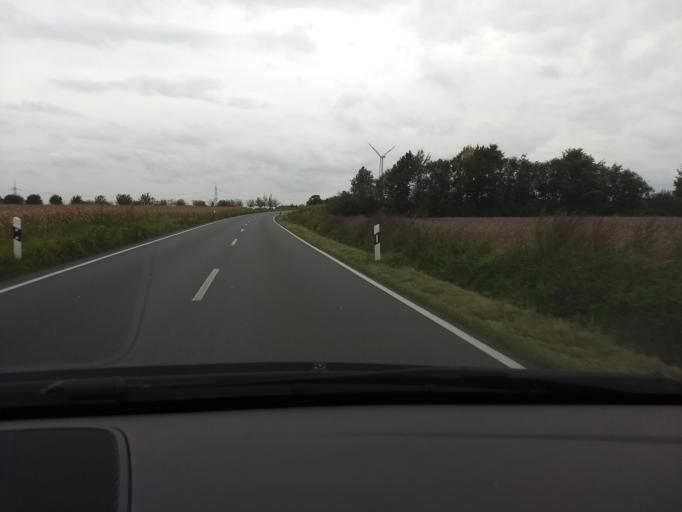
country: DE
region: North Rhine-Westphalia
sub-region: Regierungsbezirk Munster
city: Heiden
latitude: 51.8115
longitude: 6.9684
